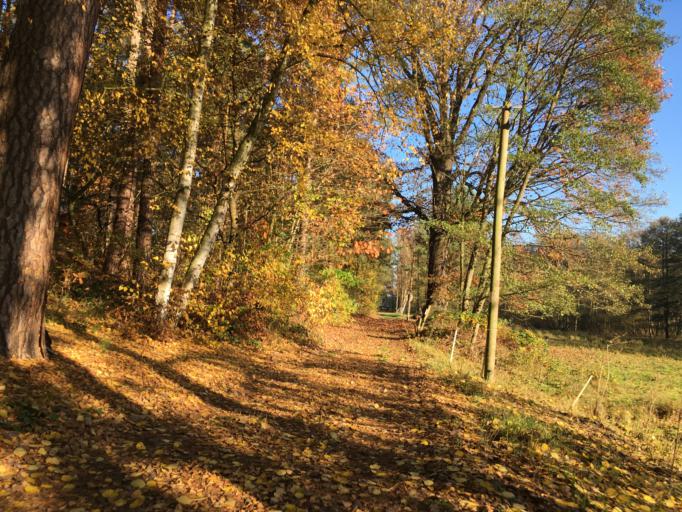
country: DE
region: Brandenburg
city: Wendisch Rietz
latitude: 52.1695
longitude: 13.9905
